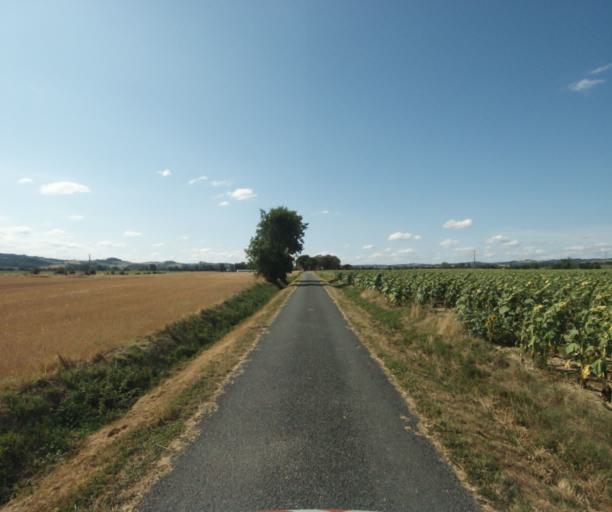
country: FR
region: Midi-Pyrenees
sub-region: Departement de la Haute-Garonne
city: Revel
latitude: 43.5087
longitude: 1.9830
